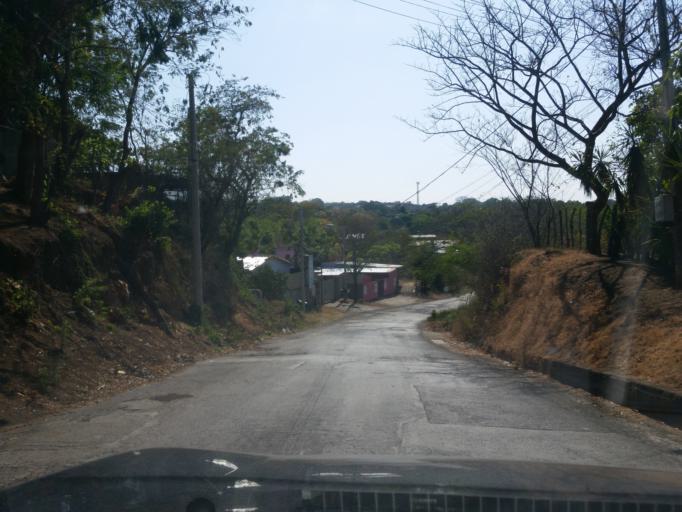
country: NI
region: Managua
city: Managua
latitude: 12.0977
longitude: -86.2946
